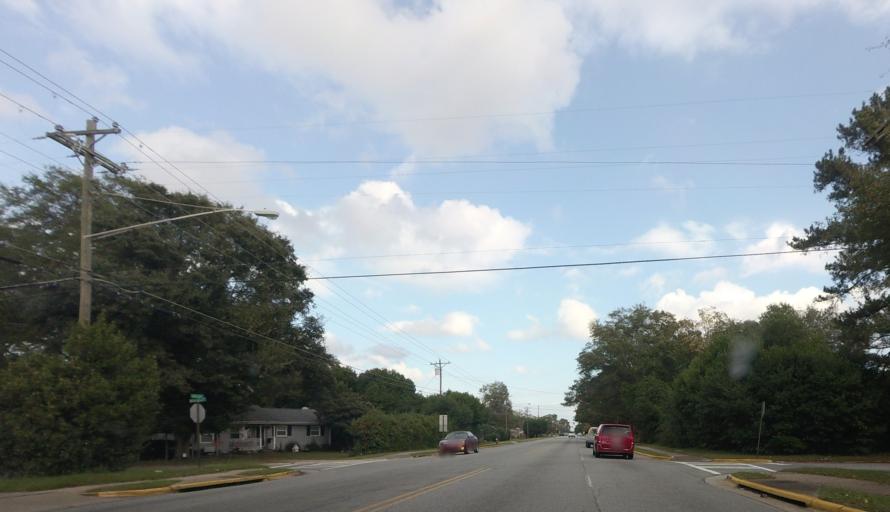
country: US
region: Georgia
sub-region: Houston County
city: Warner Robins
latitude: 32.6264
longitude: -83.6353
